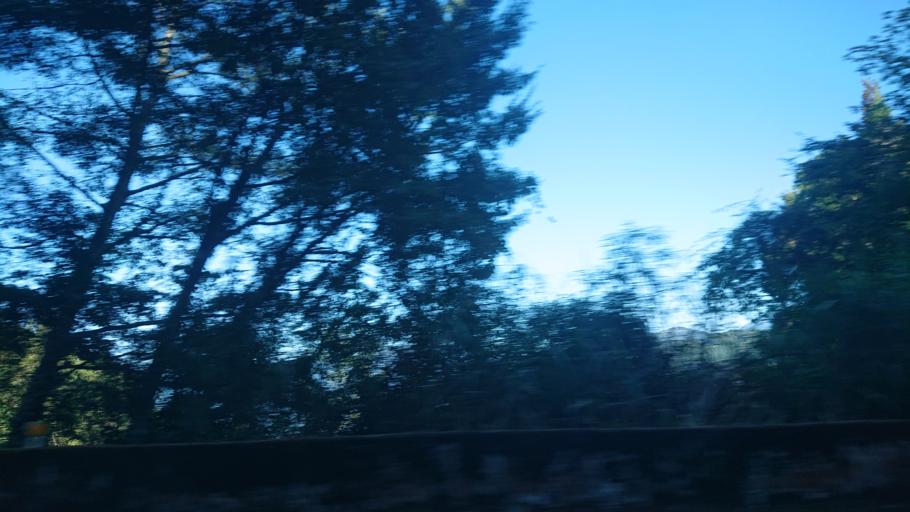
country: TW
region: Taiwan
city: Lugu
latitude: 23.4813
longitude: 120.8327
